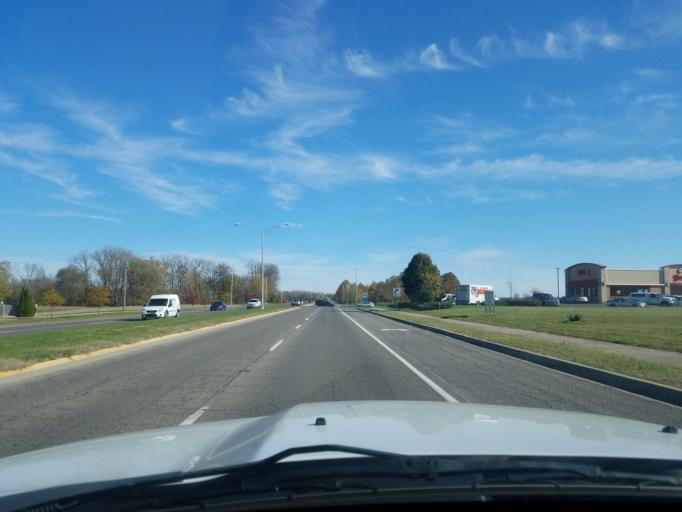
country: US
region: Indiana
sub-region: Bartholomew County
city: Columbus
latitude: 39.2001
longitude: -85.9460
